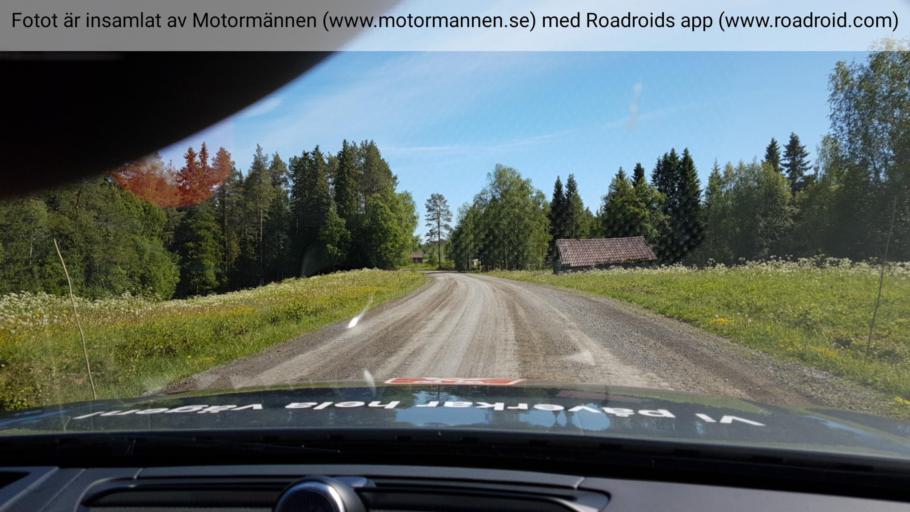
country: SE
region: Jaemtland
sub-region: OEstersunds Kommun
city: Brunflo
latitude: 63.0050
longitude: 14.7935
